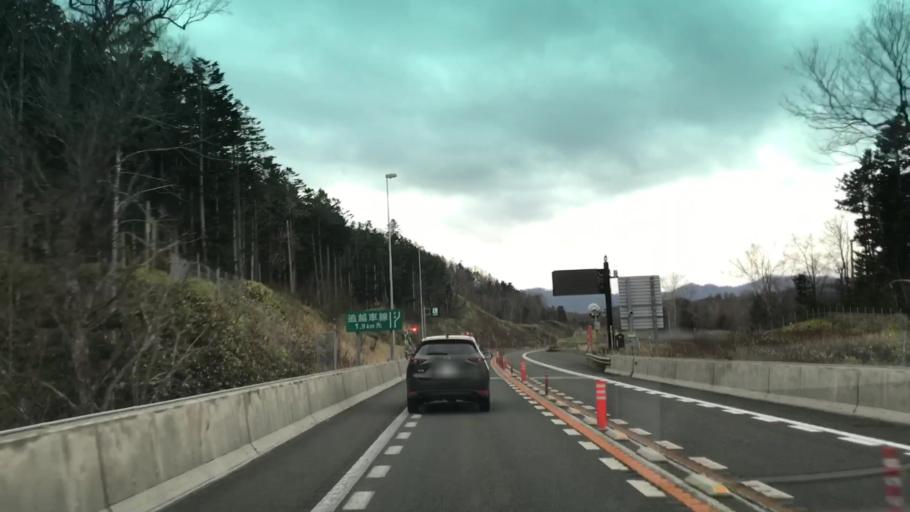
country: JP
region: Hokkaido
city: Shimo-furano
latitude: 42.9488
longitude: 142.2341
